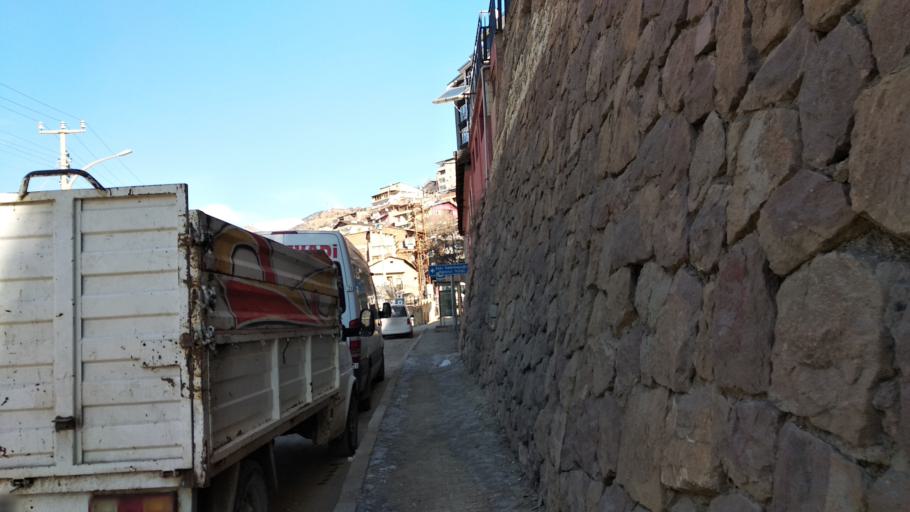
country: TR
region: Gumushane
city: Gumushkhane
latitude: 40.4537
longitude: 39.4928
